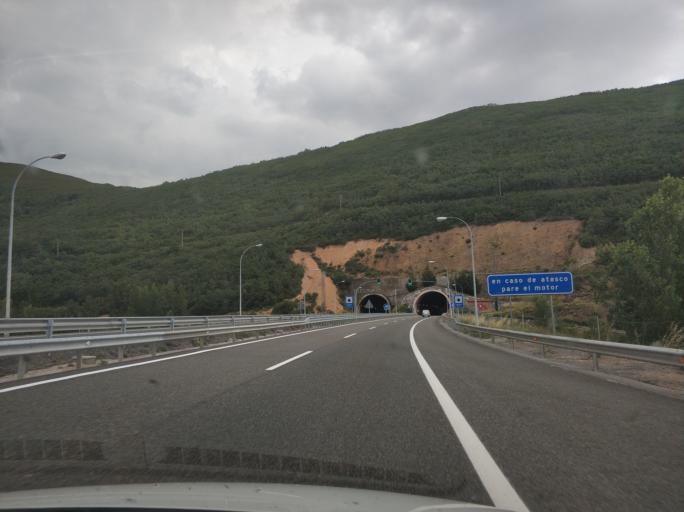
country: ES
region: Castille and Leon
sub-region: Provincia de Leon
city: Soto y Amio
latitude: 42.8454
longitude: -5.8756
